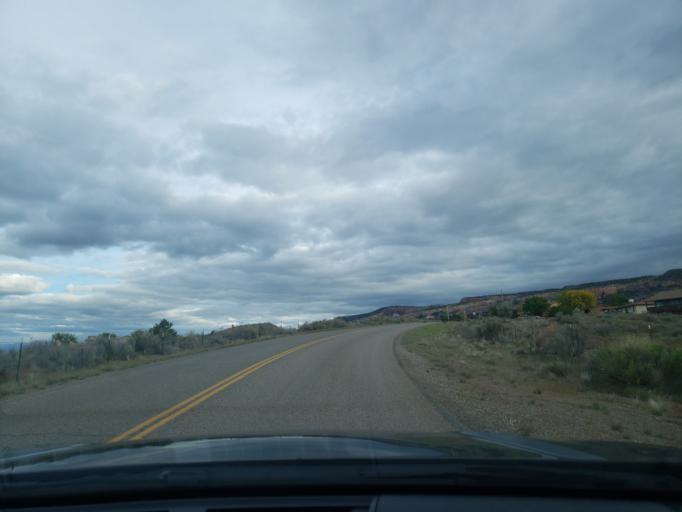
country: US
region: Colorado
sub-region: Mesa County
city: Fruita
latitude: 39.1404
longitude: -108.7428
